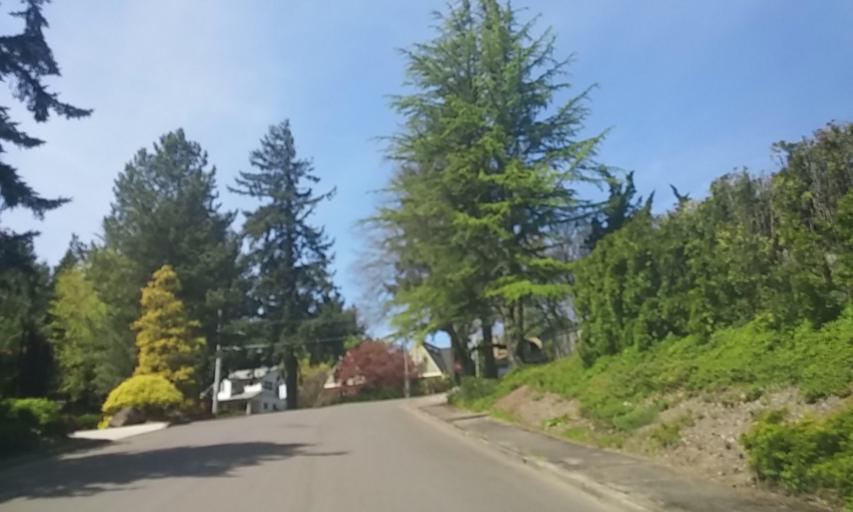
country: US
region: Oregon
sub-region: Washington County
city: West Slope
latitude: 45.5040
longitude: -122.7441
